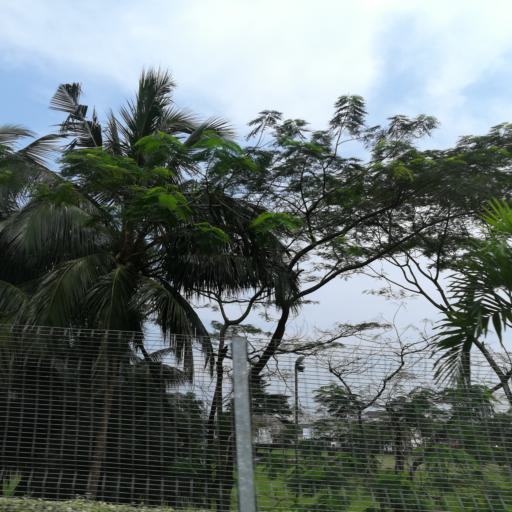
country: NG
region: Rivers
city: Port Harcourt
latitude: 4.8348
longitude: 7.0144
